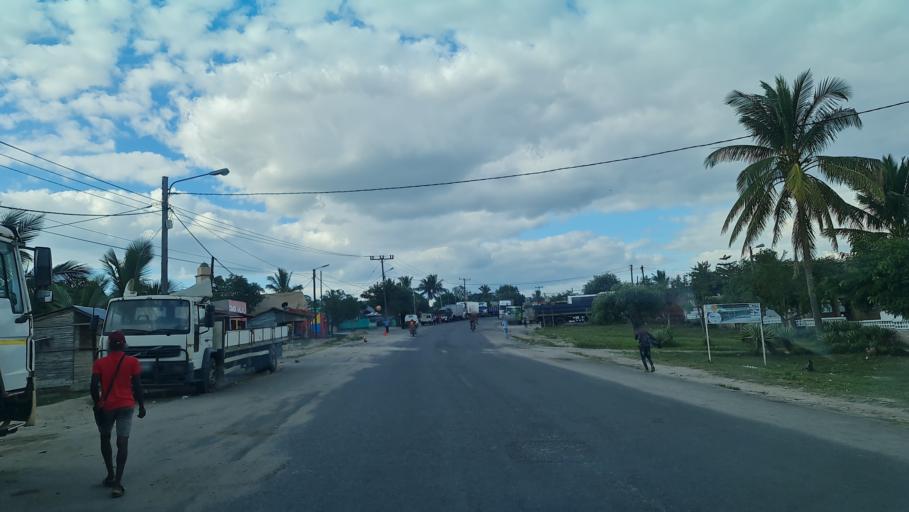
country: MZ
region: Manica
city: Chimoio
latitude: -19.2113
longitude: 33.9250
